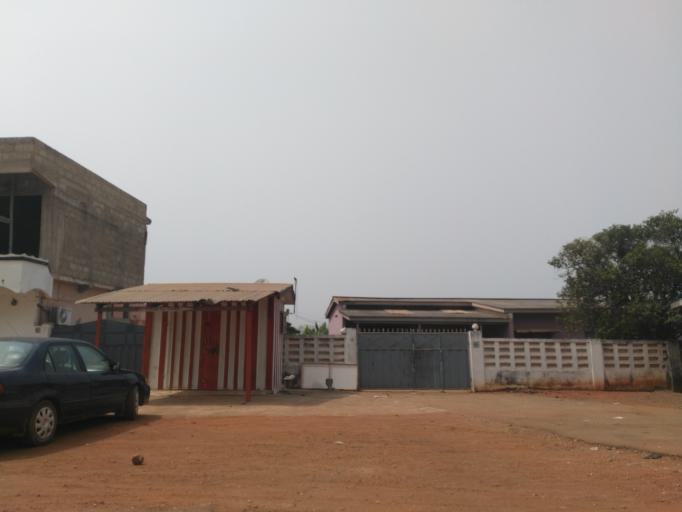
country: GH
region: Ashanti
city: Kumasi
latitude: 6.6763
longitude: -1.6436
